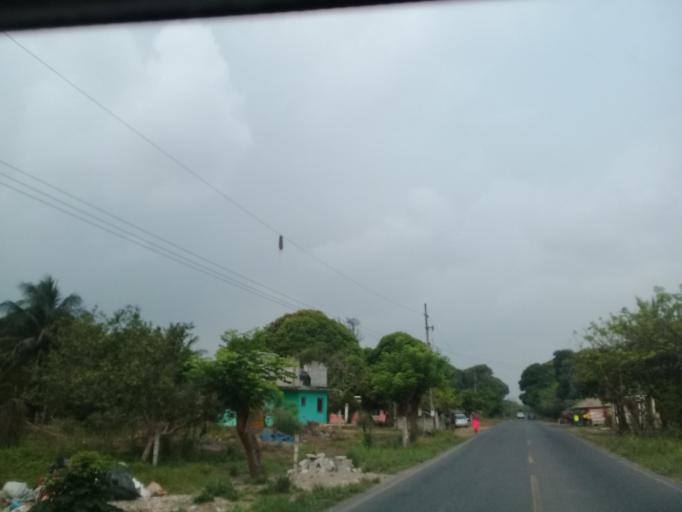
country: MX
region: Veracruz
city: El Tejar
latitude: 19.0547
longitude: -96.1926
